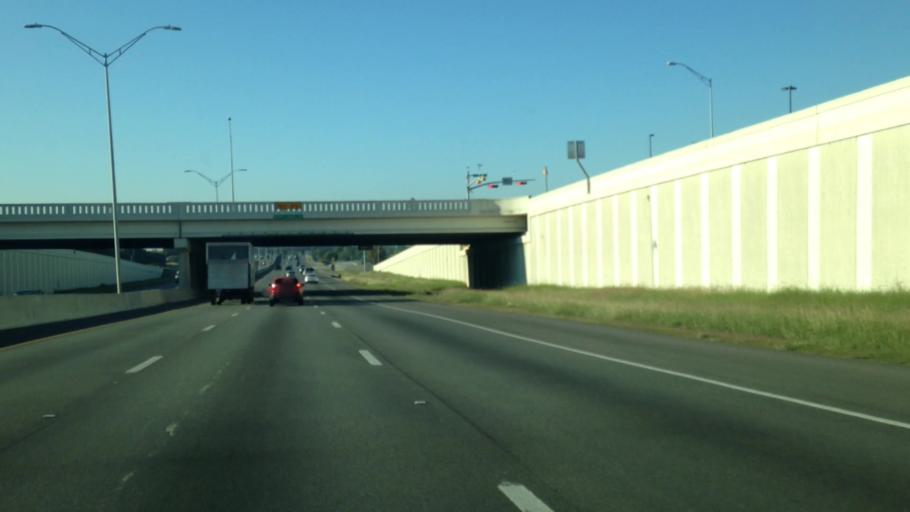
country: US
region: Texas
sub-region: Bexar County
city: Kirby
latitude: 29.4623
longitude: -98.4103
